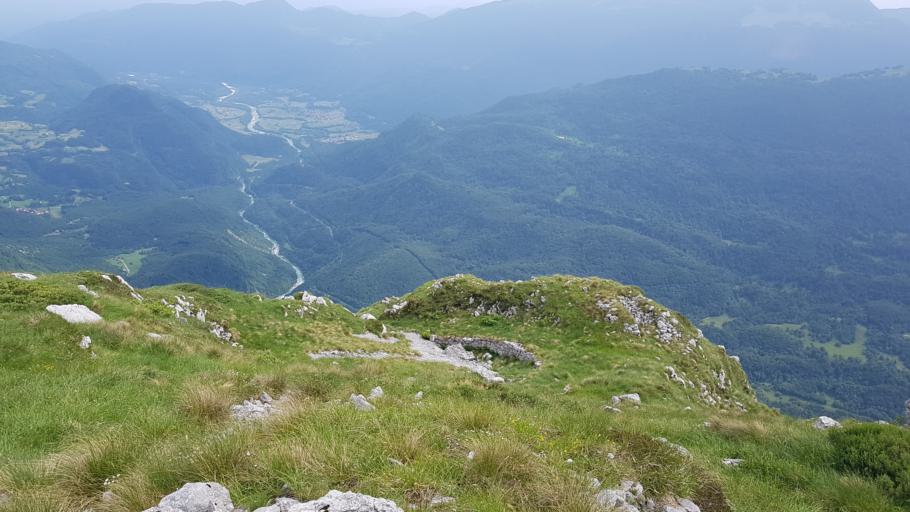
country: SI
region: Bovec
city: Bovec
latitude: 46.2977
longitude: 13.5564
